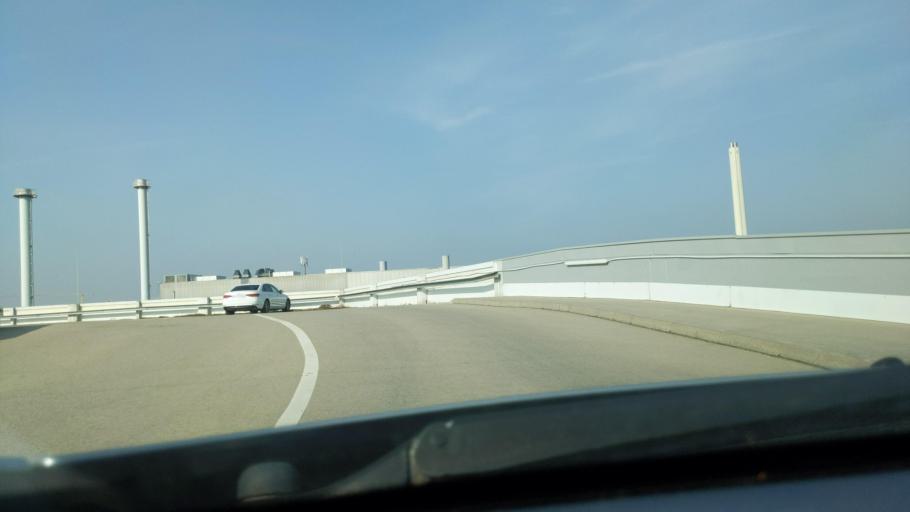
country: DE
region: Baden-Wuerttemberg
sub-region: Regierungsbezirk Stuttgart
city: Sindelfingen
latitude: 48.6962
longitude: 9.0064
